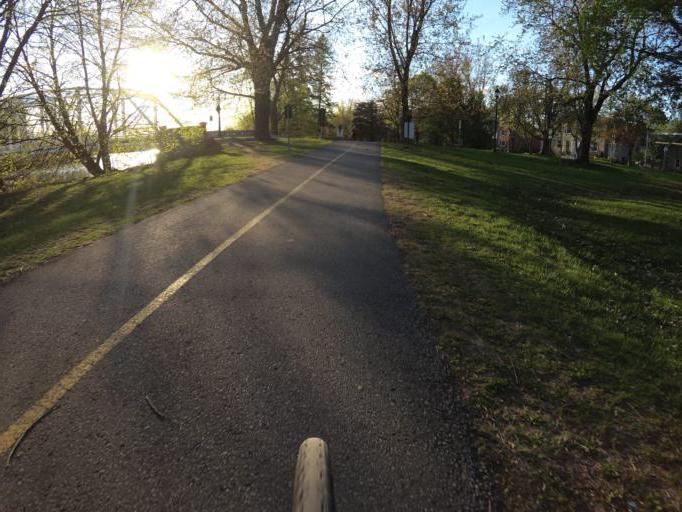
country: CA
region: Ontario
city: Ottawa
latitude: 45.4400
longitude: -75.6901
